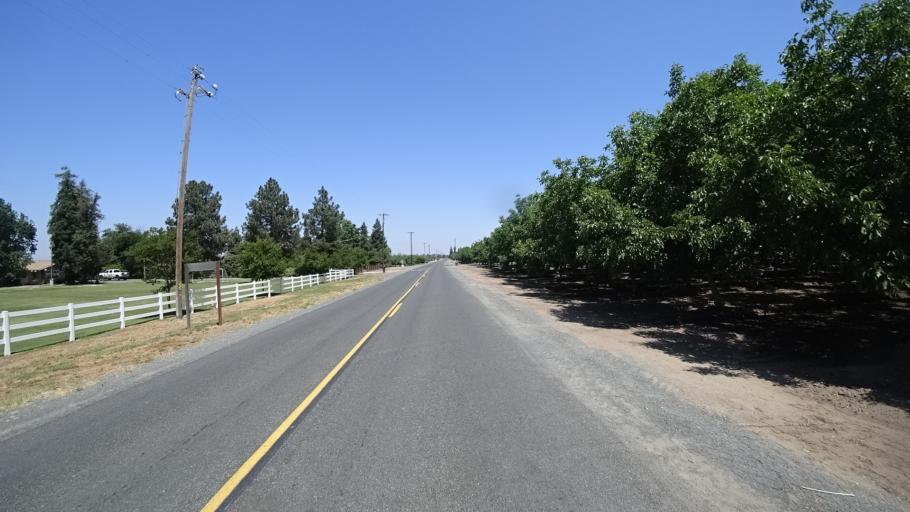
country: US
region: California
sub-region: Kings County
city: Lucerne
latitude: 36.4022
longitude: -119.6730
